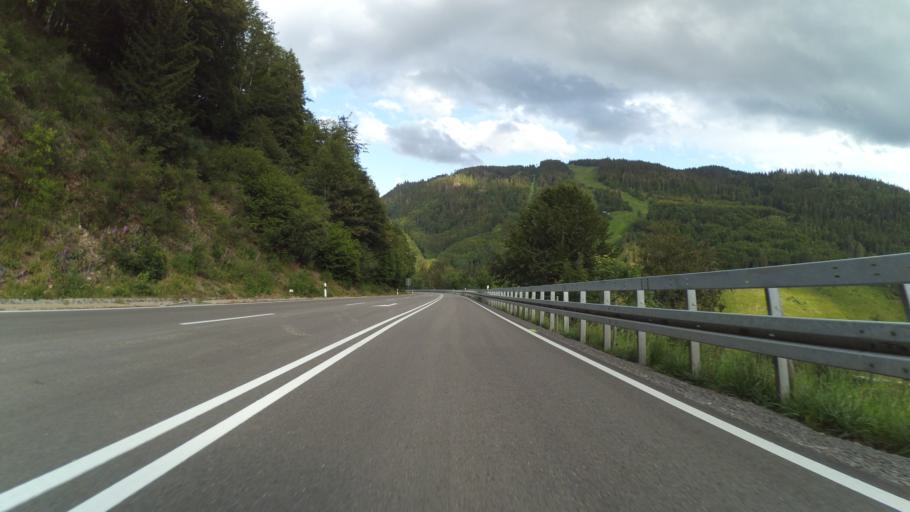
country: DE
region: Baden-Wuerttemberg
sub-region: Freiburg Region
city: Todtnau
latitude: 47.8582
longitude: 7.9997
